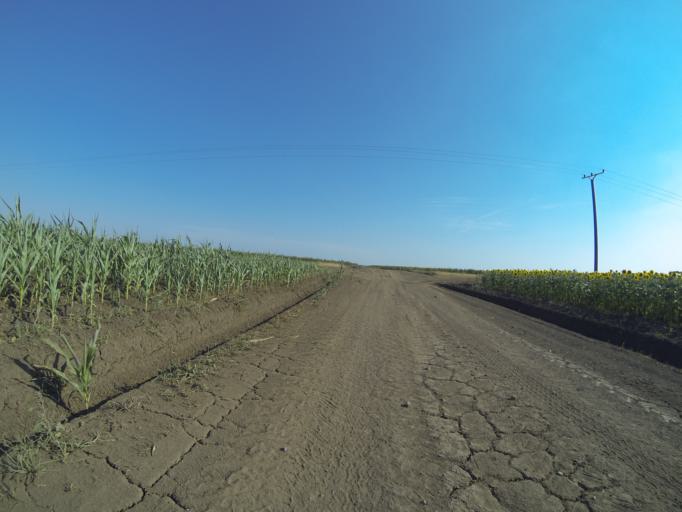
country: RO
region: Dolj
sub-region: Comuna Segarcea
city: Segarcea
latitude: 44.0674
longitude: 23.7316
